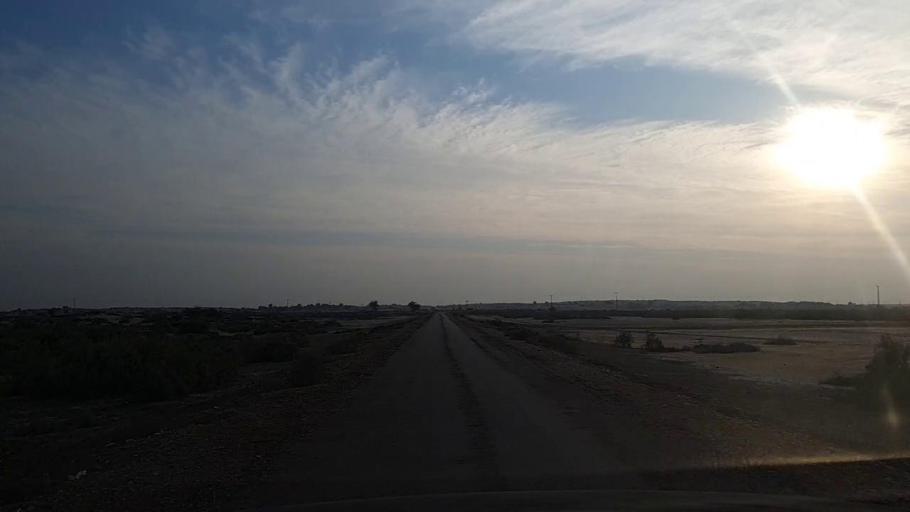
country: PK
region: Sindh
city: Jam Sahib
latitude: 26.4040
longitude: 68.5069
